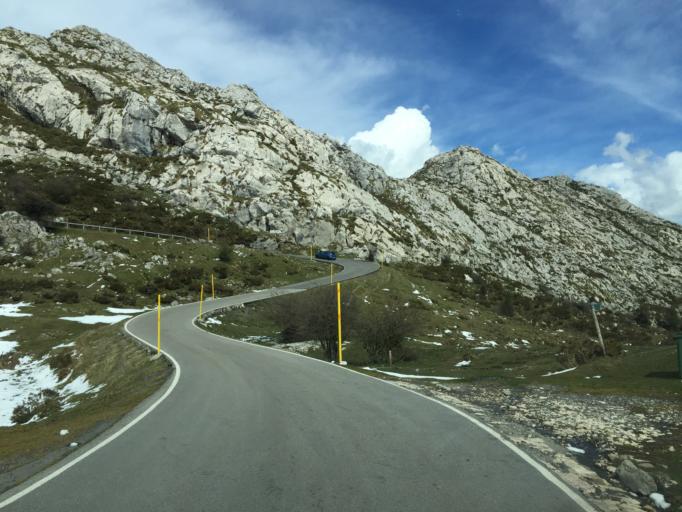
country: ES
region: Asturias
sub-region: Province of Asturias
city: Amieva
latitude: 43.2820
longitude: -5.0036
